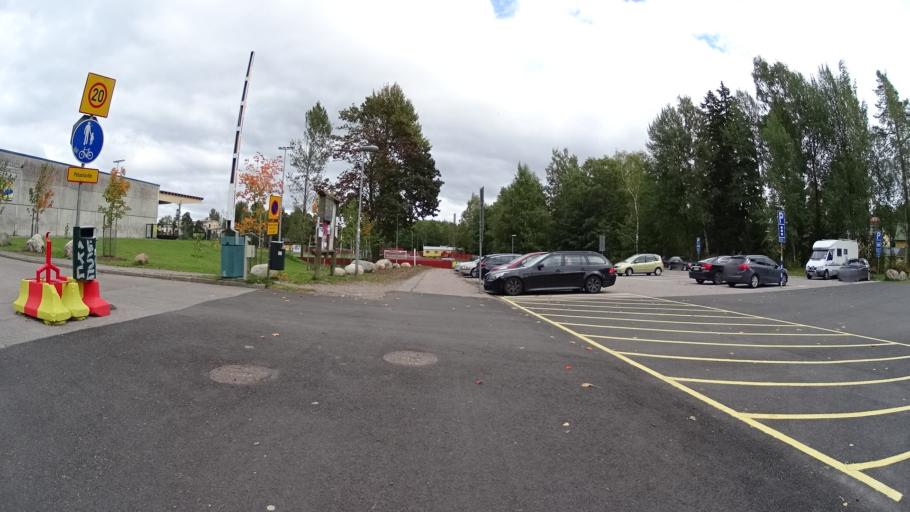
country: FI
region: Uusimaa
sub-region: Helsinki
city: Helsinki
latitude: 60.2337
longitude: 24.9611
